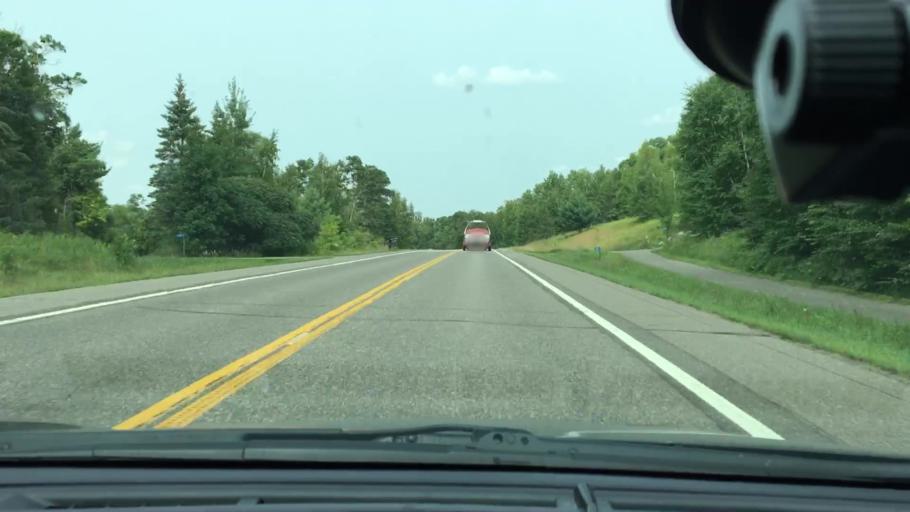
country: US
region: Minnesota
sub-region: Cass County
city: East Gull Lake
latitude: 46.3978
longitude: -94.3513
